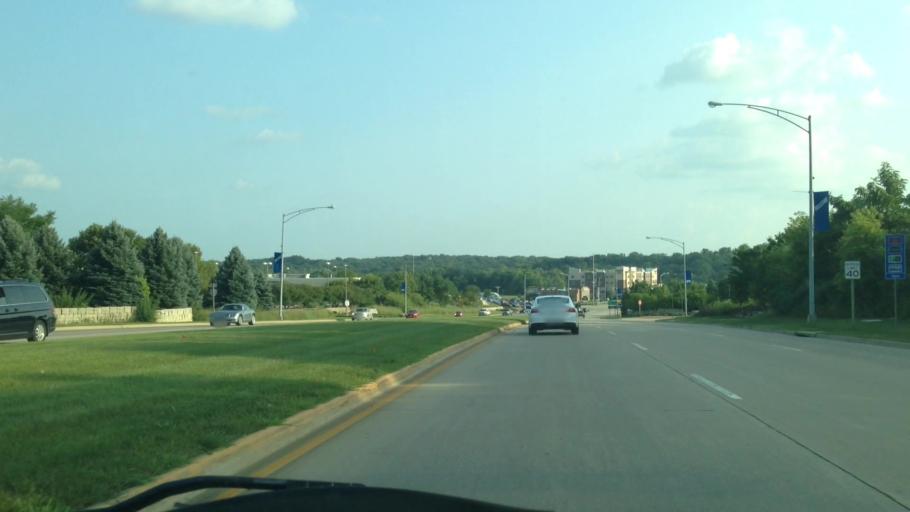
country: US
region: Iowa
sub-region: Johnson County
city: Coralville
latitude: 41.6915
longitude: -91.6087
